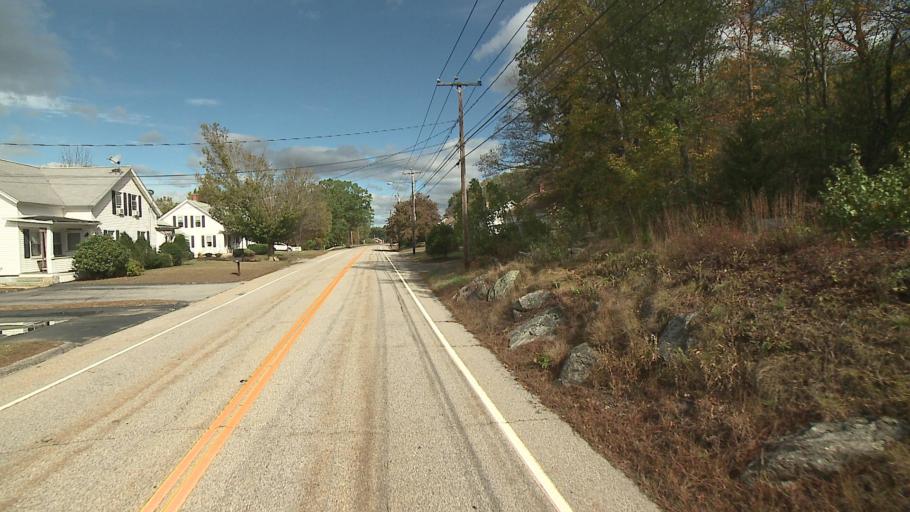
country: US
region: Connecticut
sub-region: Windham County
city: Putnam
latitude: 41.9374
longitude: -71.8947
